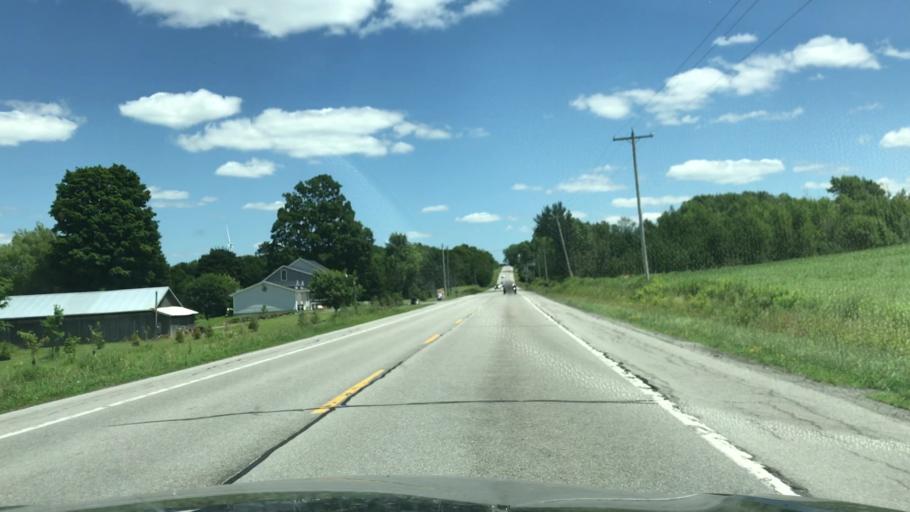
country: US
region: New York
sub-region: Wyoming County
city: Attica
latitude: 42.7536
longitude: -78.2660
